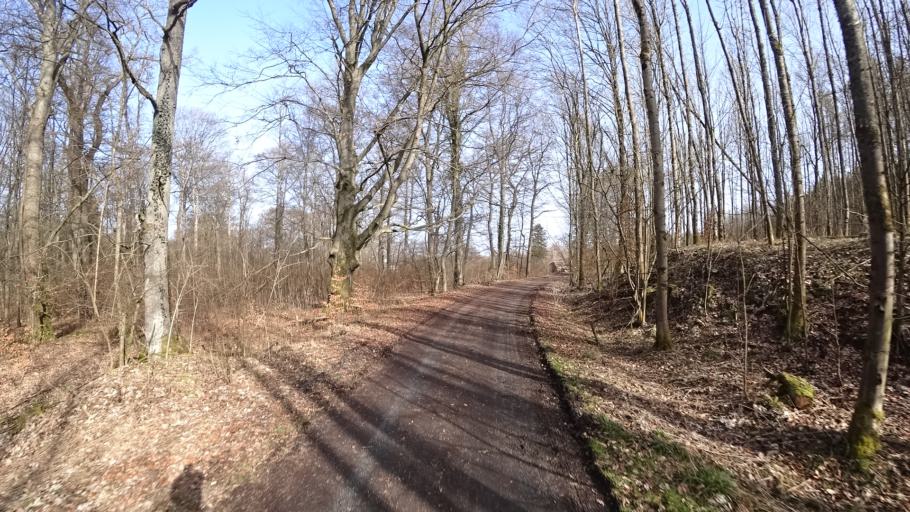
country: DE
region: Rheinland-Pfalz
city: Dickendorf
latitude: 50.7249
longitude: 7.8525
